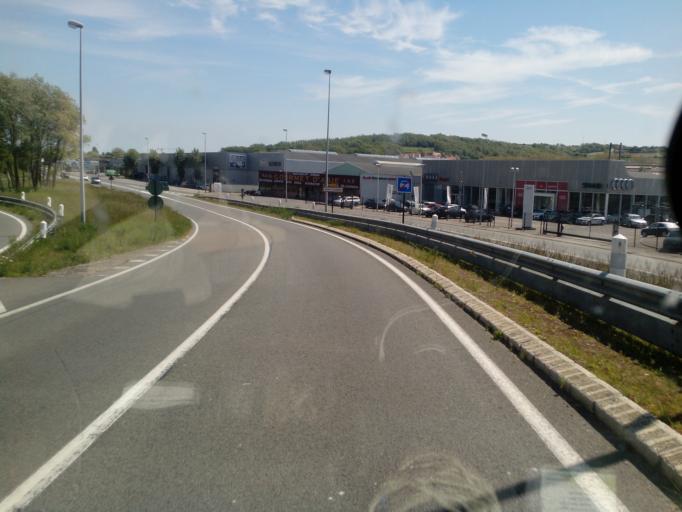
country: FR
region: Nord-Pas-de-Calais
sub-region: Departement du Pas-de-Calais
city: Saint-Leonard
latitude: 50.6939
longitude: 1.6099
